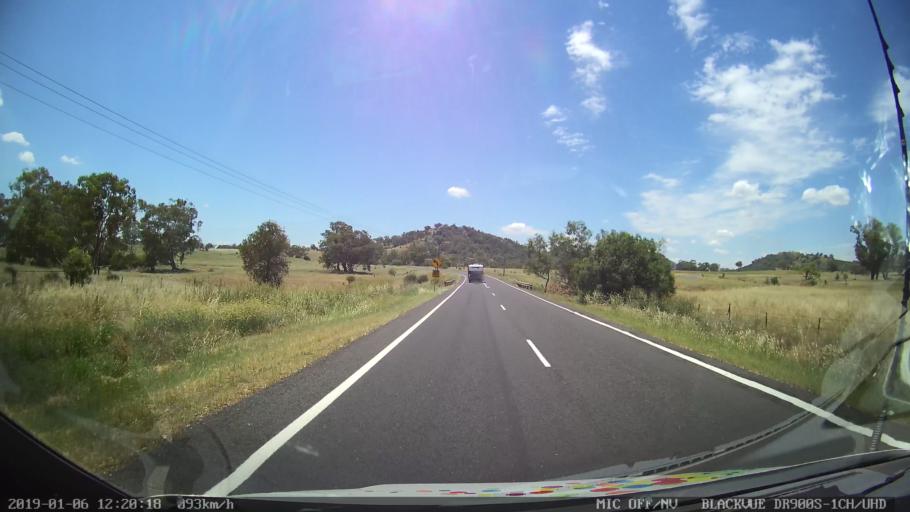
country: AU
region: New South Wales
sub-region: Tamworth Municipality
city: Phillip
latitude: -31.2750
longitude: 150.7678
